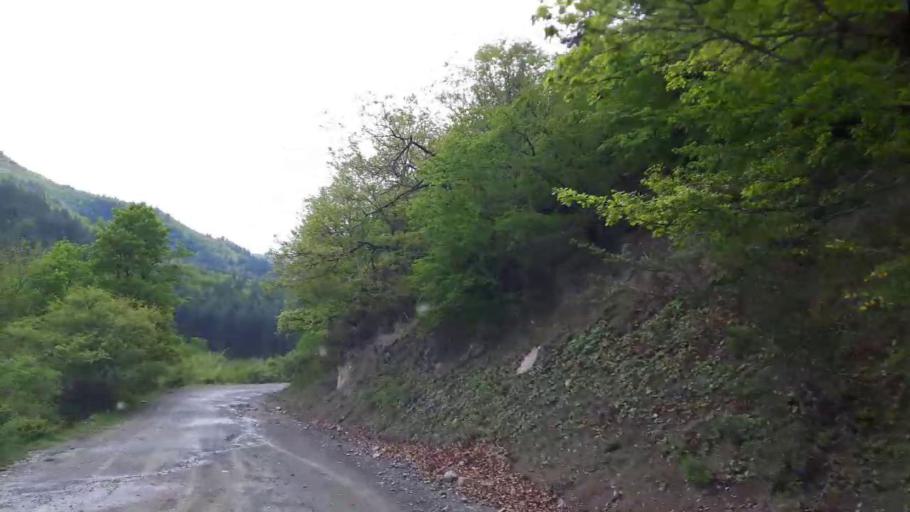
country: GE
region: Shida Kartli
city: Gori
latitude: 41.8763
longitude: 43.9894
